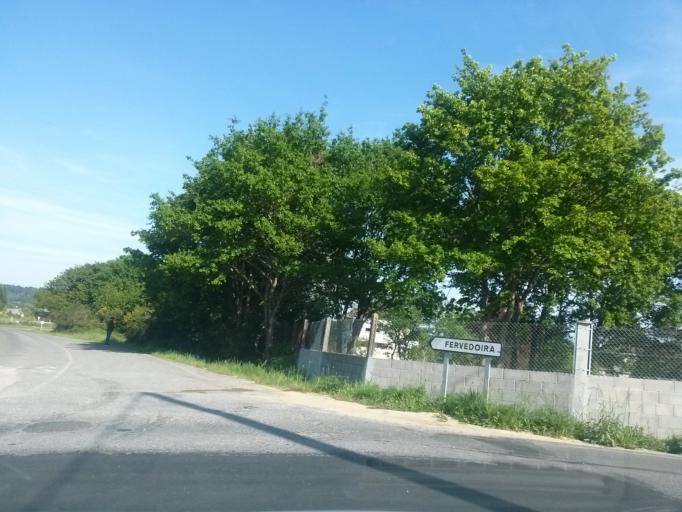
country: ES
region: Galicia
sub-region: Provincia de Lugo
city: Lugo
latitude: 43.0331
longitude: -7.5483
